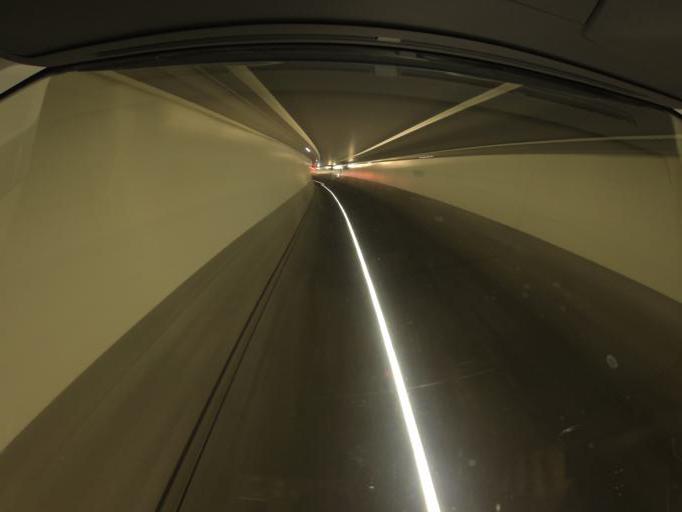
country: CH
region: Zurich
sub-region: Bezirk Hinwil
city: Rueti / Dorfzentrum, Suedl. Teil
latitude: 47.2420
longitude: 8.8613
